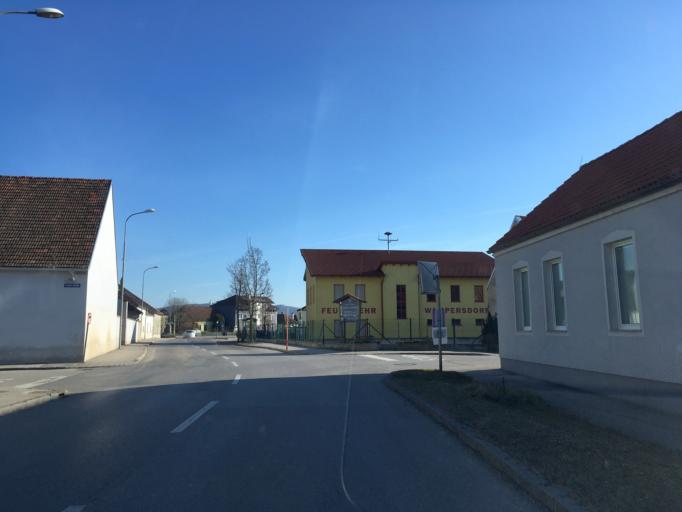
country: AT
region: Burgenland
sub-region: Eisenstadt-Umgebung
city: Wimpassing an der Leitha
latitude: 47.9234
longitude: 16.4272
